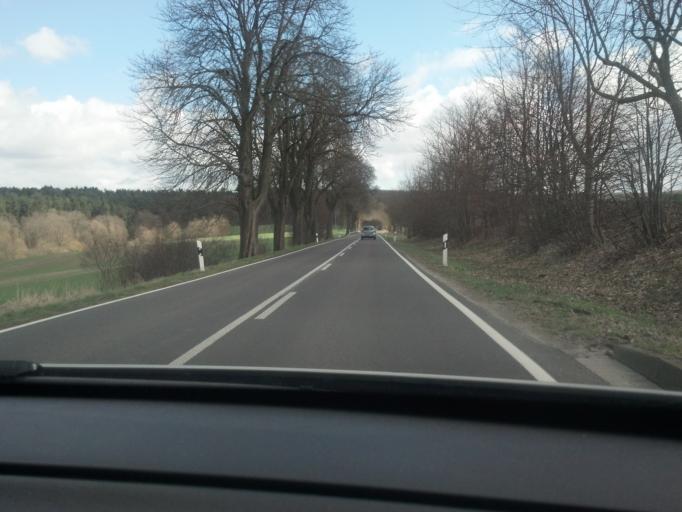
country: DE
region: Mecklenburg-Vorpommern
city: Loitz
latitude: 53.3640
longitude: 13.3864
